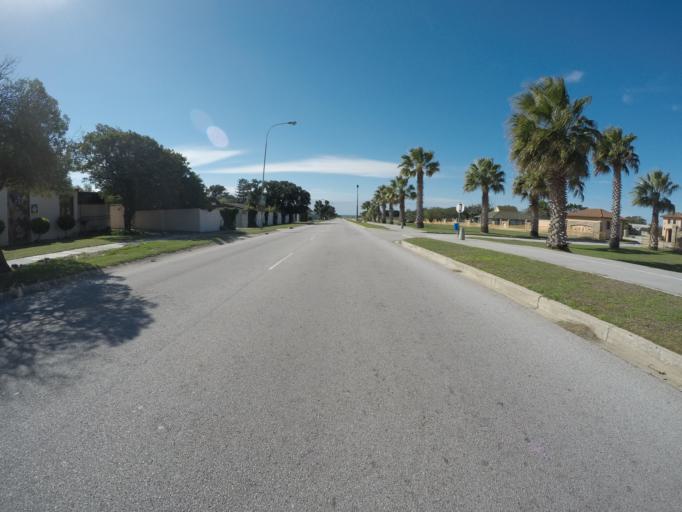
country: ZA
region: Eastern Cape
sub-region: Nelson Mandela Bay Metropolitan Municipality
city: Port Elizabeth
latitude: -33.9967
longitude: 25.6650
